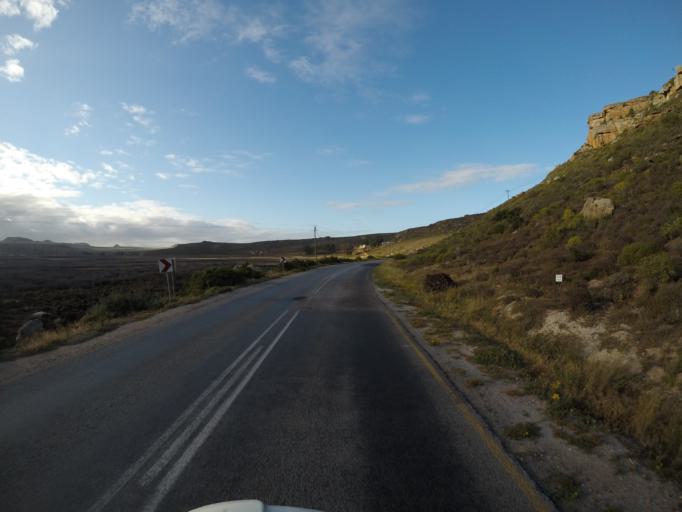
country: ZA
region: Western Cape
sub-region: West Coast District Municipality
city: Clanwilliam
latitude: -32.3175
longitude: 18.3577
